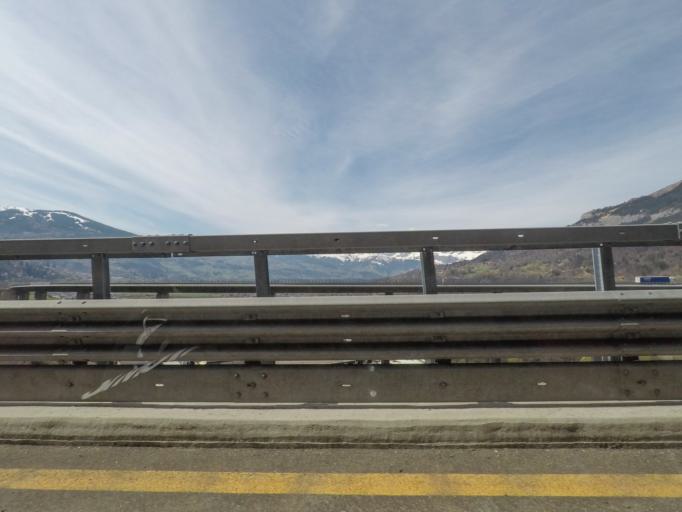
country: FR
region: Rhone-Alpes
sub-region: Departement de la Haute-Savoie
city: Saint-Gervais-les-Bains
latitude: 45.9288
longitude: 6.7352
